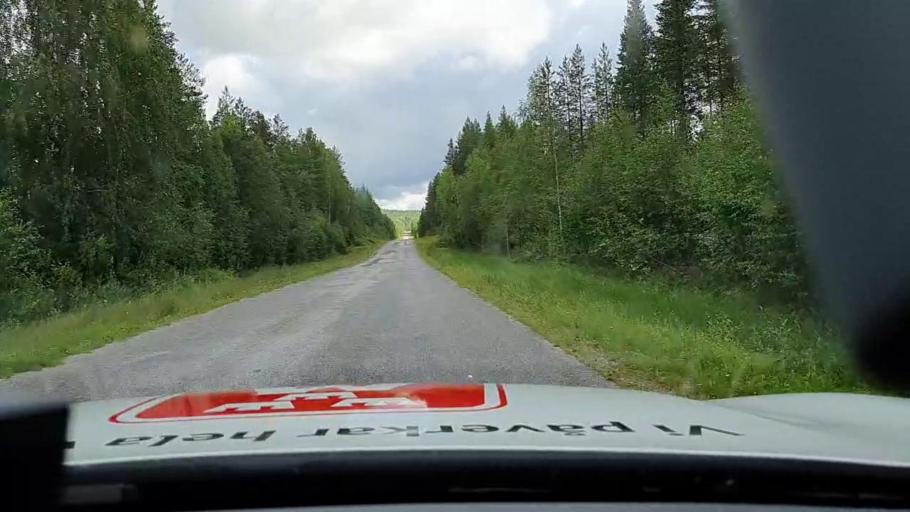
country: SE
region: Norrbotten
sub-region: Overkalix Kommun
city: OEverkalix
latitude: 66.2516
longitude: 23.0131
